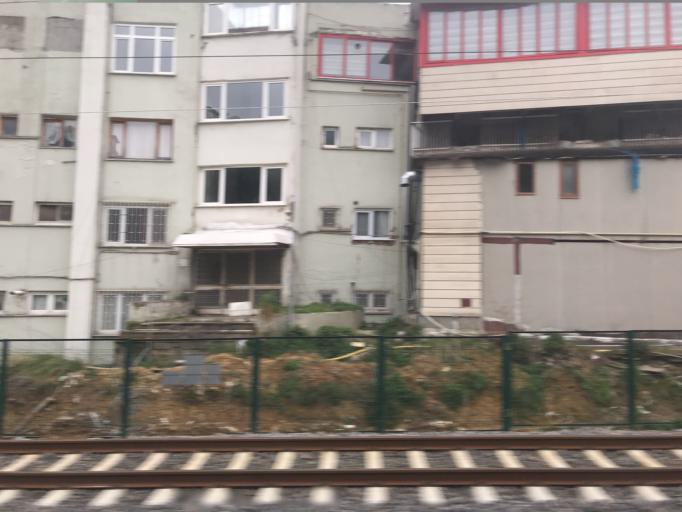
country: TR
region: Istanbul
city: Maltepe
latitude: 40.9286
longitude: 29.1224
